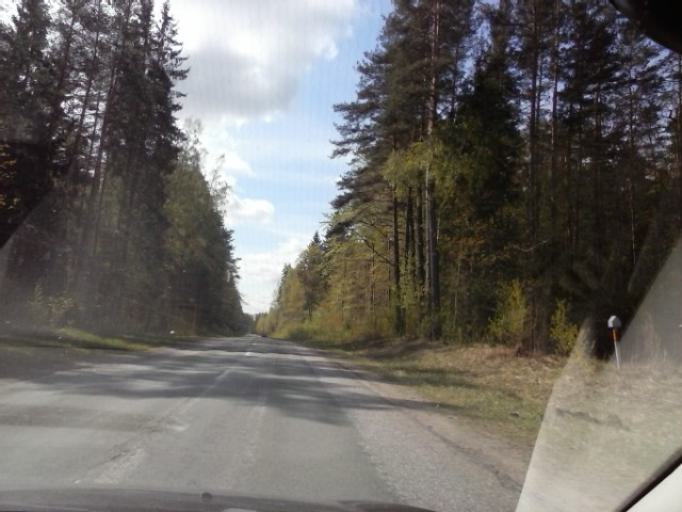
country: LV
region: Sigulda
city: Sigulda
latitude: 57.2058
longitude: 24.8520
